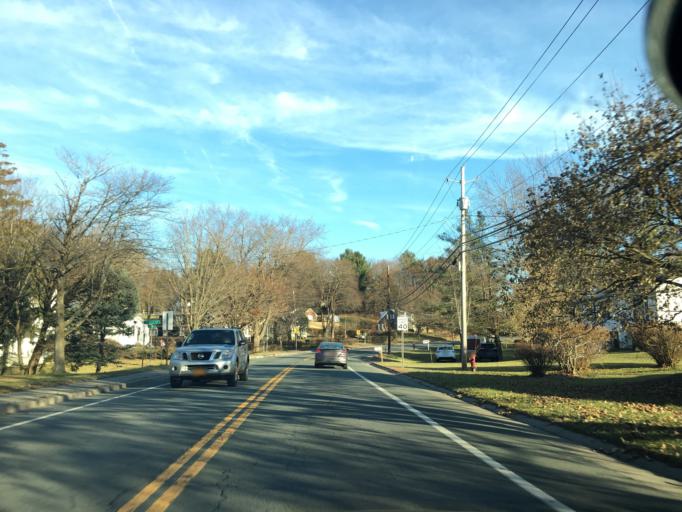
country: US
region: New York
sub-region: Rensselaer County
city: Wynantskill
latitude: 42.6918
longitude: -73.6462
